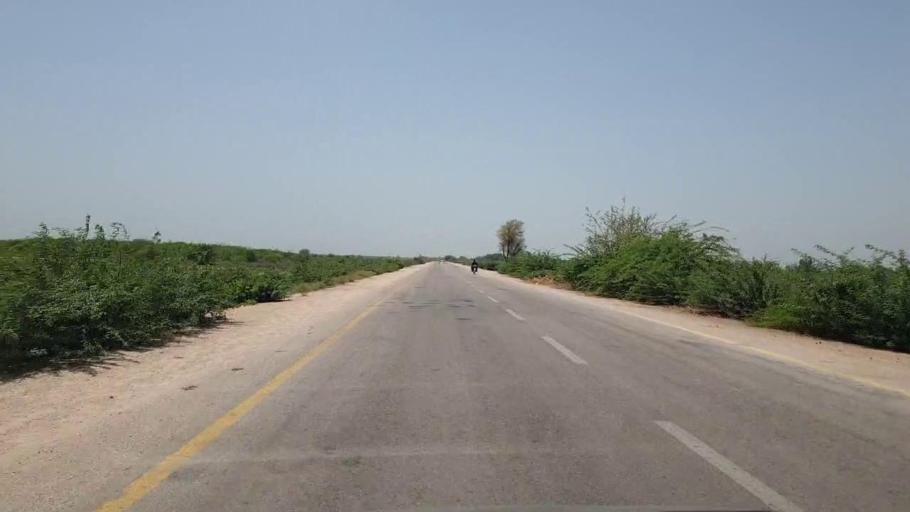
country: PK
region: Sindh
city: Sakrand
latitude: 26.1359
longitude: 68.3732
